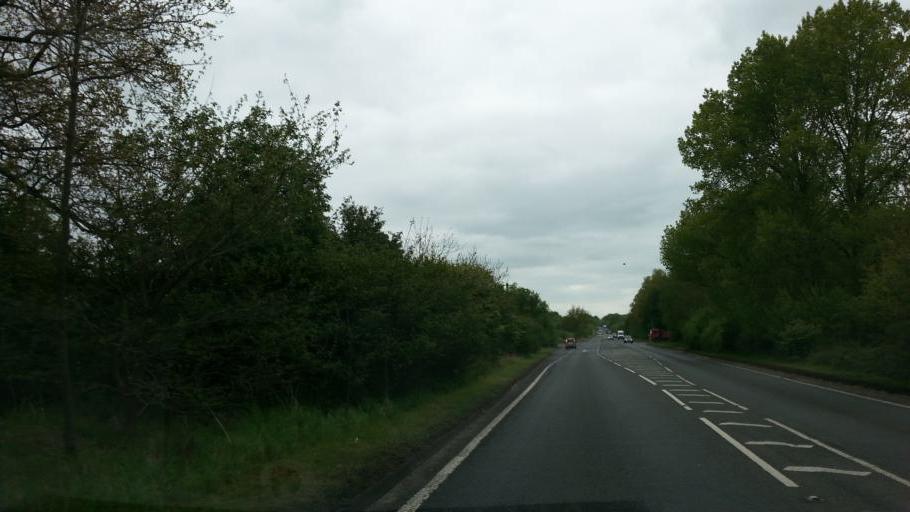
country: GB
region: England
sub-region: Suffolk
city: Hadleigh
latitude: 52.0551
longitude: 0.9546
